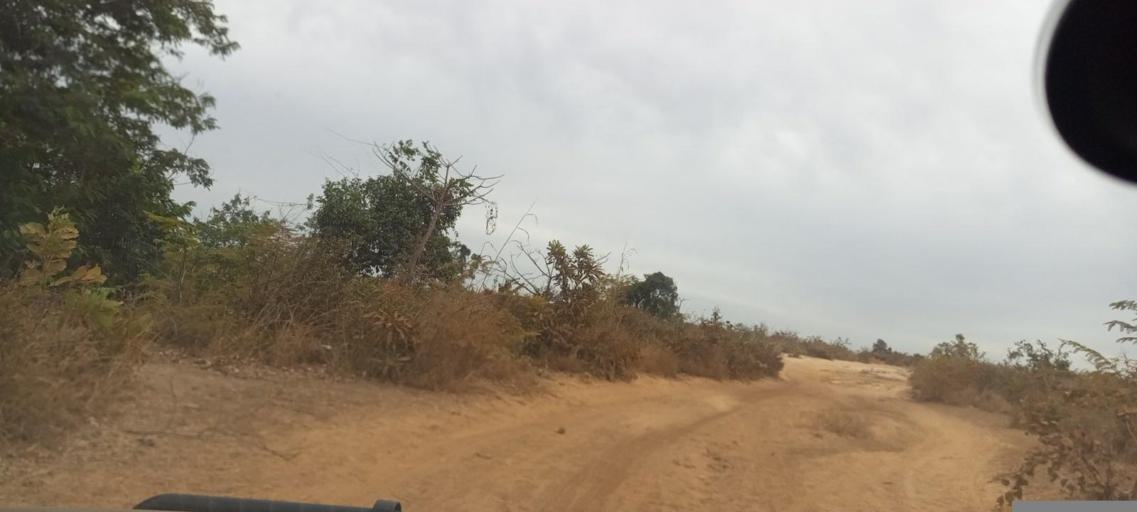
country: ML
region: Koulikoro
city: Kati
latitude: 12.7898
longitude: -8.2558
